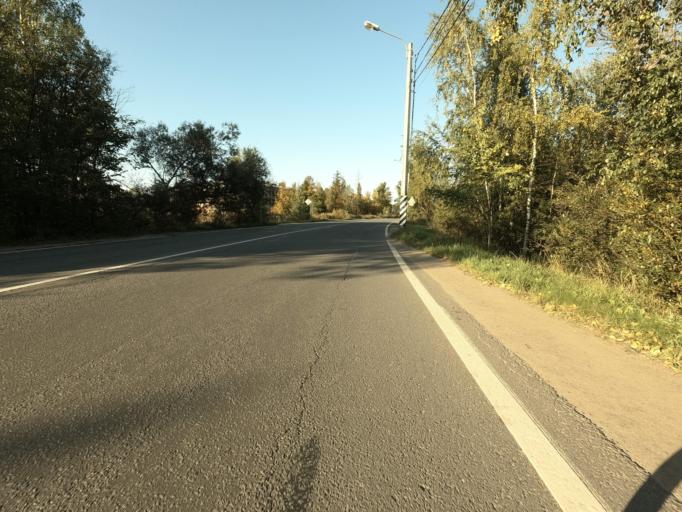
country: RU
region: St.-Petersburg
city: Kolpino
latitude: 59.7548
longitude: 30.6159
